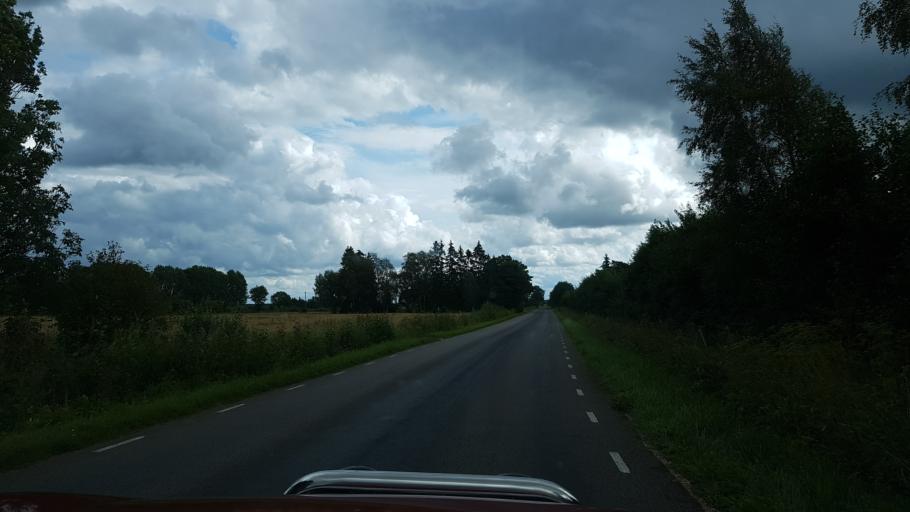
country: EE
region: Laeaene
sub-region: Lihula vald
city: Lihula
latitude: 58.7220
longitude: 23.9685
